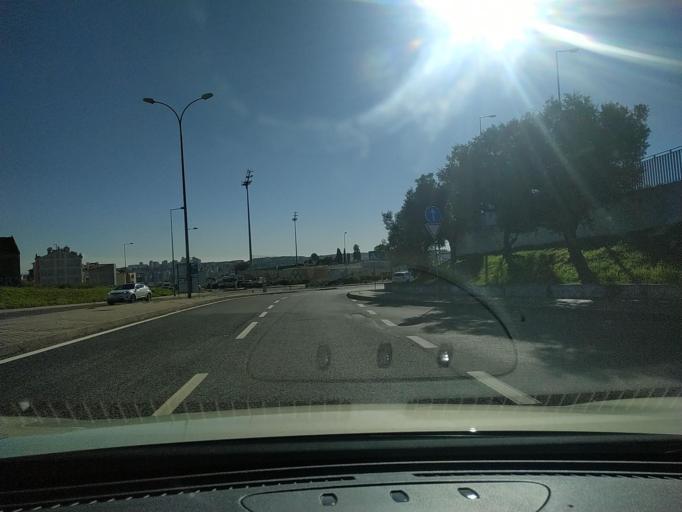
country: PT
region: Lisbon
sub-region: Amadora
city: Amadora
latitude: 38.7695
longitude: -9.2240
